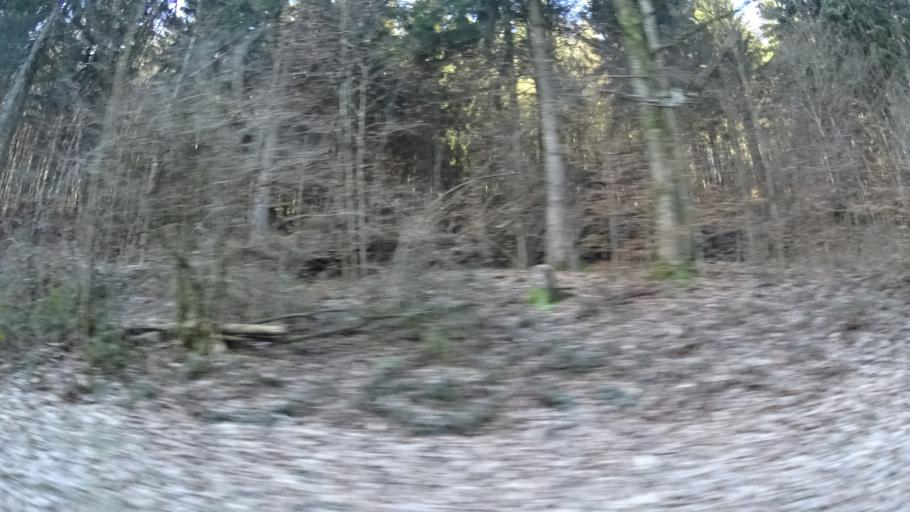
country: DE
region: Thuringia
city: Judenbach
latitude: 50.3725
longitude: 11.2163
